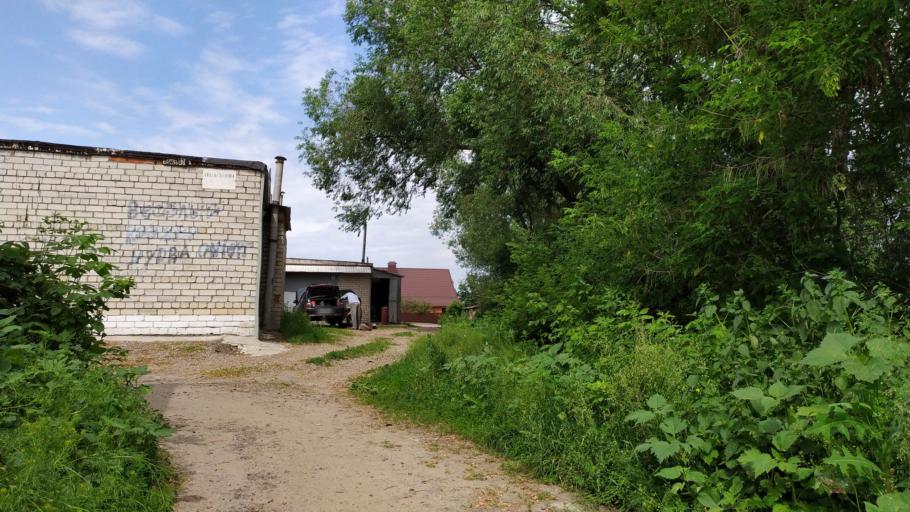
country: RU
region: Kursk
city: Kursk
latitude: 51.6628
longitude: 36.1526
